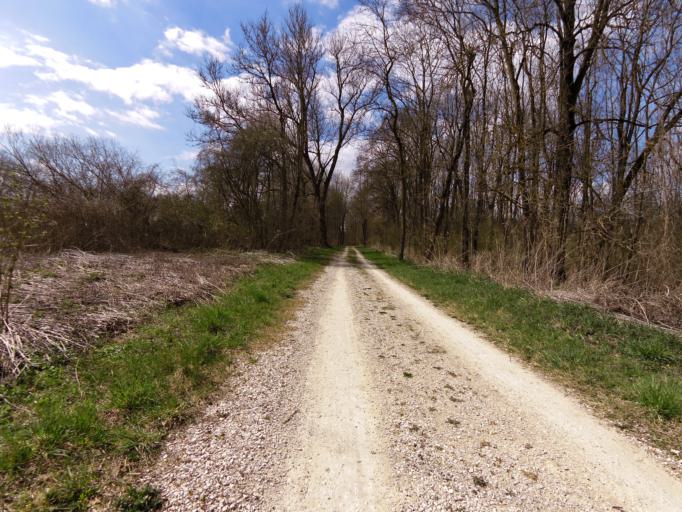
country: DE
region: Bavaria
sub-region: Lower Bavaria
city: Eching
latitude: 48.5068
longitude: 12.0636
